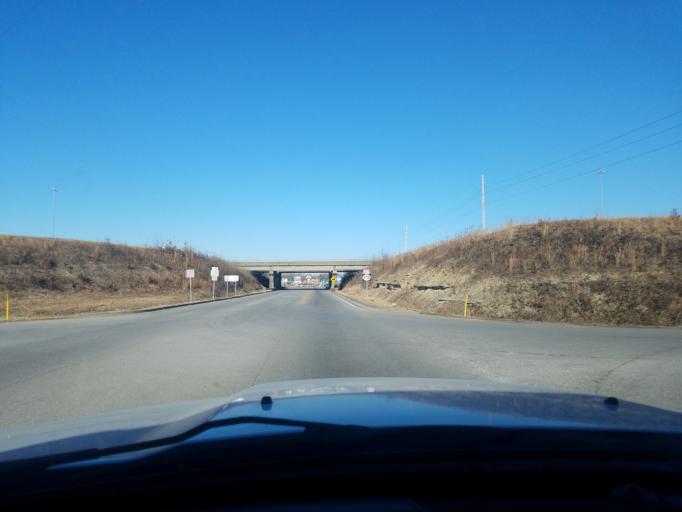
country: US
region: Kentucky
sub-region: Ohio County
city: Beaver Dam
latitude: 37.3666
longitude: -86.8416
